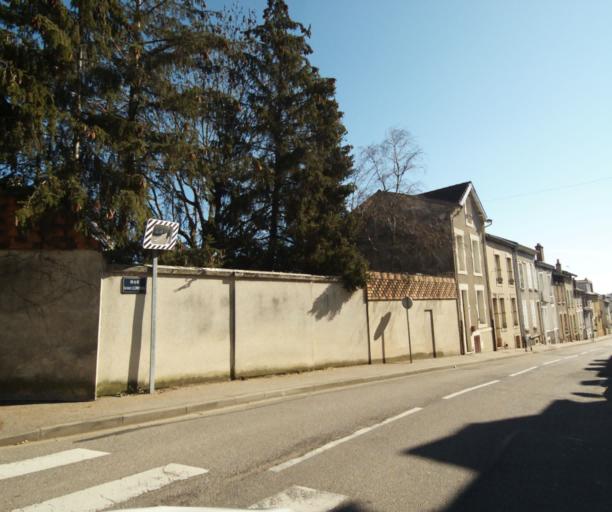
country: FR
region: Lorraine
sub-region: Departement de Meurthe-et-Moselle
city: Saint-Max
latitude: 48.7034
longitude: 6.2049
